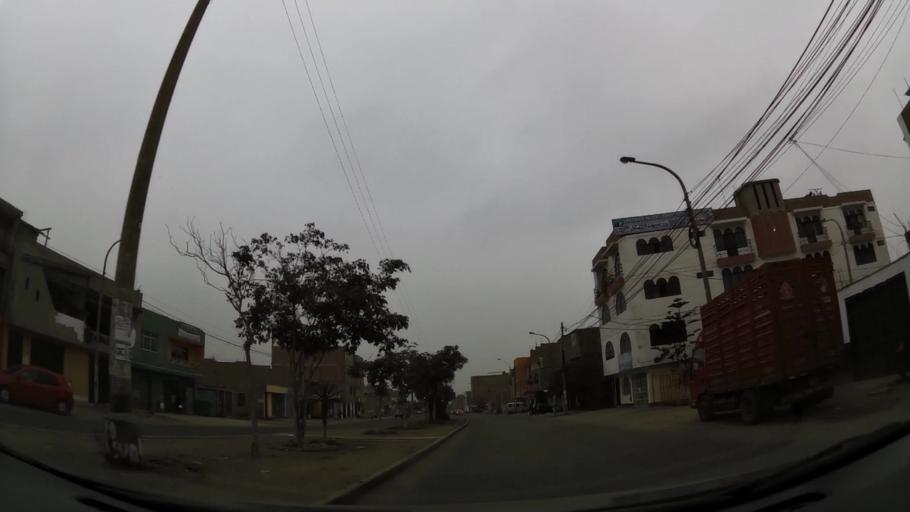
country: PE
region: Lima
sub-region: Lima
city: Urb. Santo Domingo
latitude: -11.9217
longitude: -77.0541
